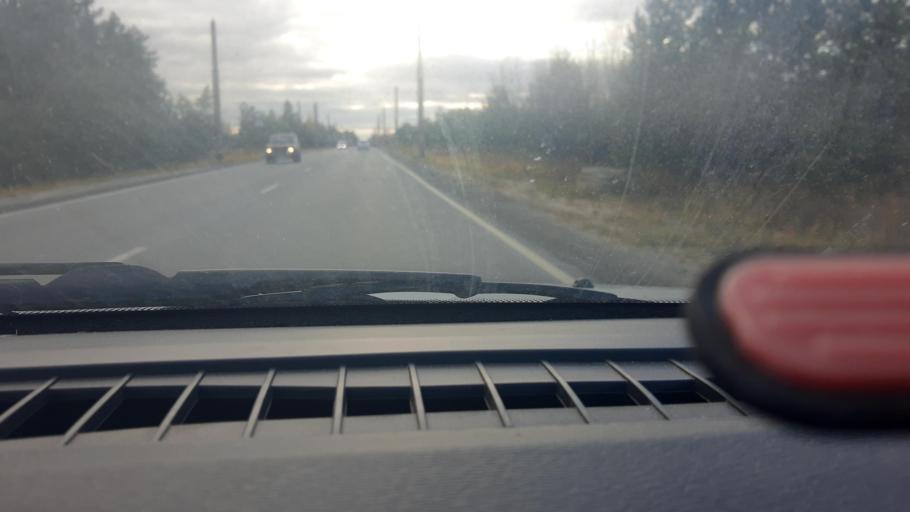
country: RU
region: Nizjnij Novgorod
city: Babino
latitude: 56.2722
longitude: 43.5477
